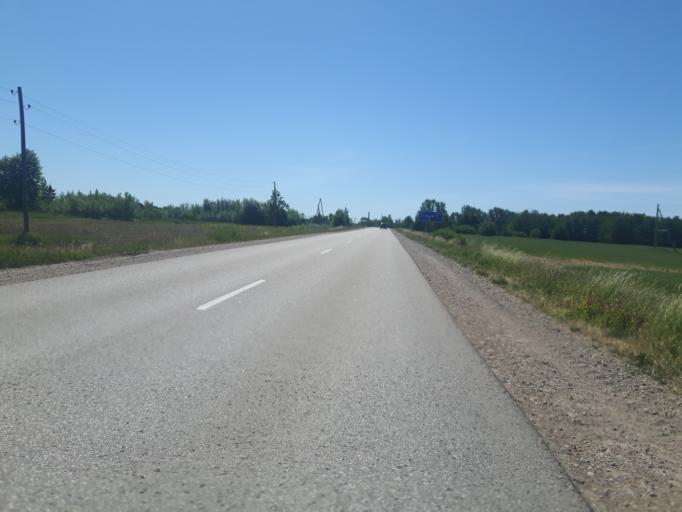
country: LV
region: Durbe
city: Liegi
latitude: 56.5695
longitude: 21.2710
